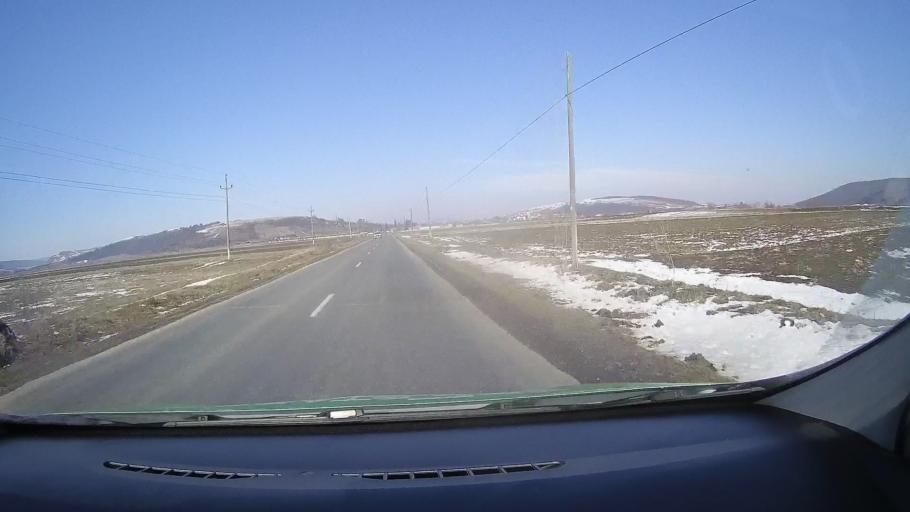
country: RO
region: Brasov
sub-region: Comuna Homorod
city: Homorod
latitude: 46.0272
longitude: 25.2740
